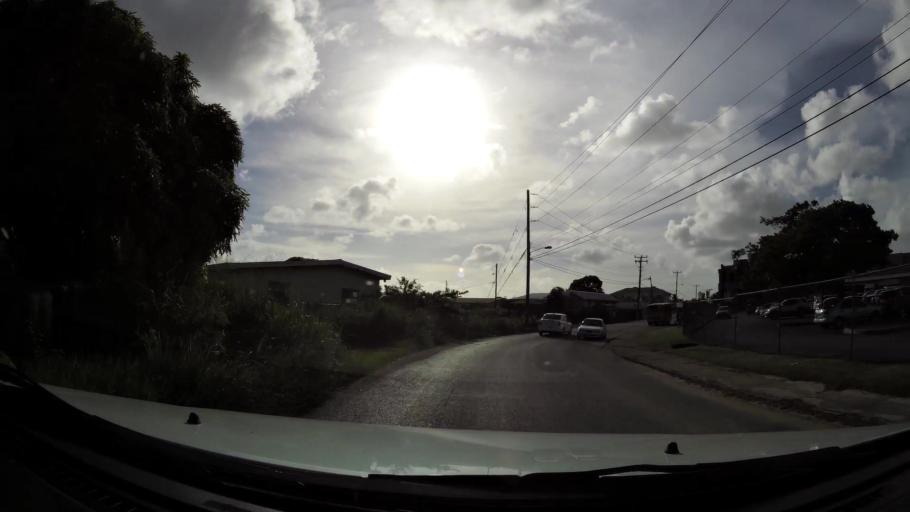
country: BB
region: Christ Church
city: Oistins
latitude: 13.0824
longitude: -59.5658
